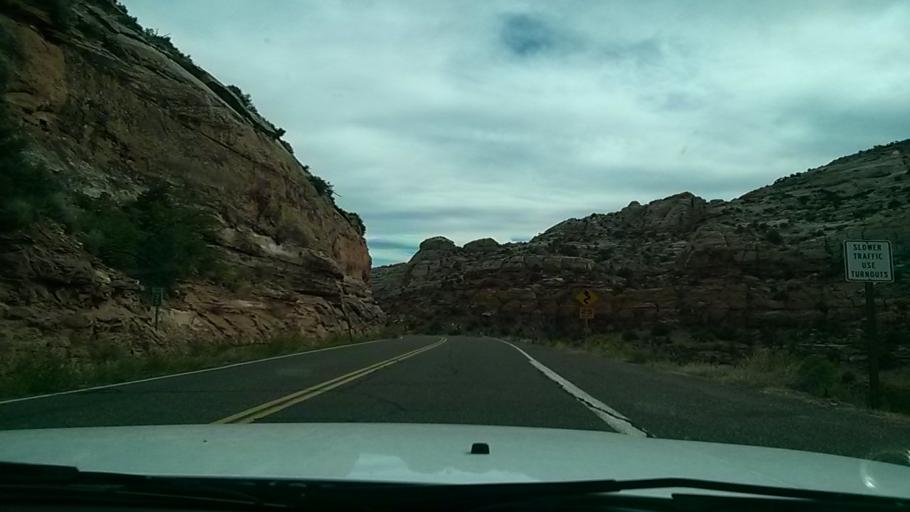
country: US
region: Utah
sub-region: Wayne County
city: Loa
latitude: 37.7928
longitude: -111.4138
